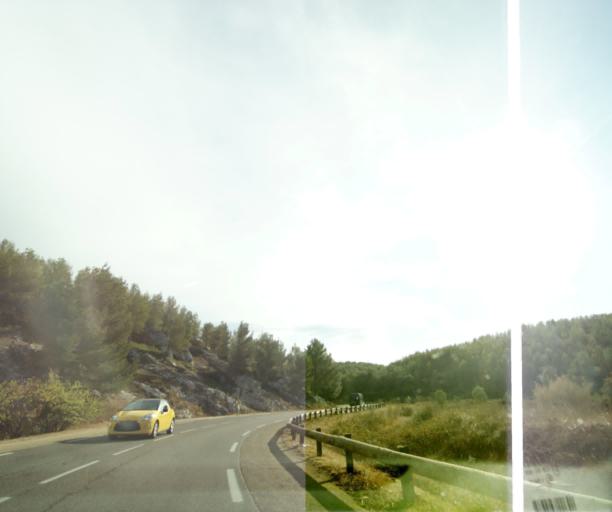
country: FR
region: Provence-Alpes-Cote d'Azur
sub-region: Departement des Bouches-du-Rhone
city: Sausset-les-Pins
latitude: 43.3483
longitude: 5.1030
